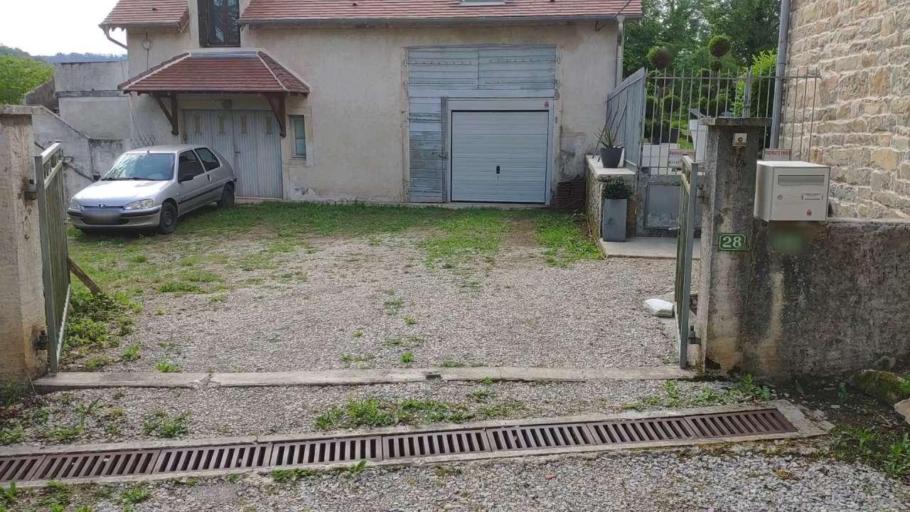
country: FR
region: Franche-Comte
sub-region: Departement du Jura
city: Perrigny
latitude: 46.7639
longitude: 5.6009
